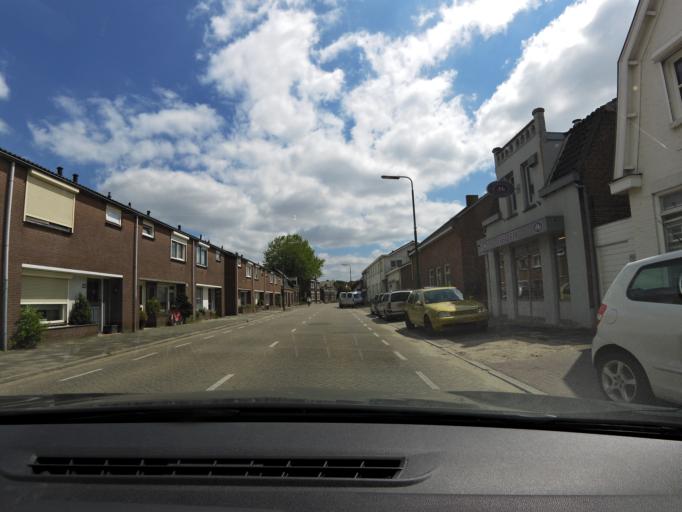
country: NL
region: North Brabant
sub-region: Gemeente Loon op Zand
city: Loon op Zand
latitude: 51.6281
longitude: 5.0674
